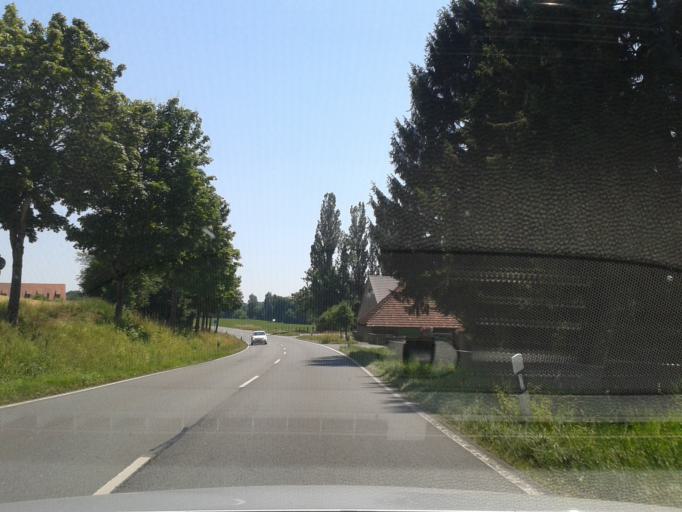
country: DE
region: North Rhine-Westphalia
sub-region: Regierungsbezirk Detmold
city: Dorentrup
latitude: 52.0306
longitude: 9.0230
